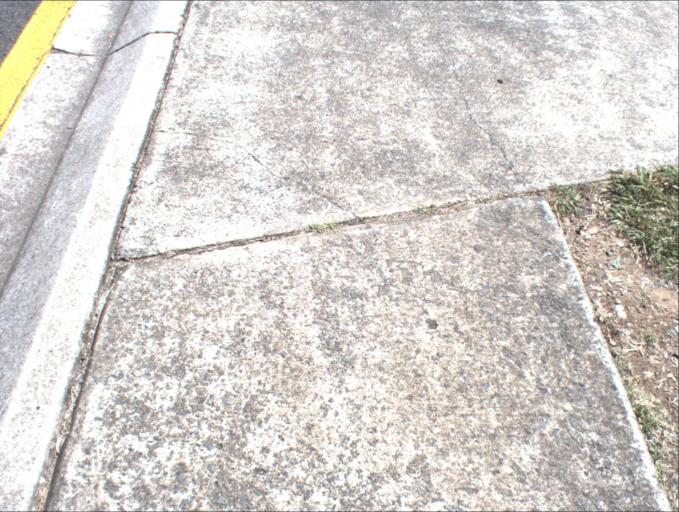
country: AU
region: Queensland
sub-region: Logan
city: Rochedale South
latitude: -27.6016
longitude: 153.1101
